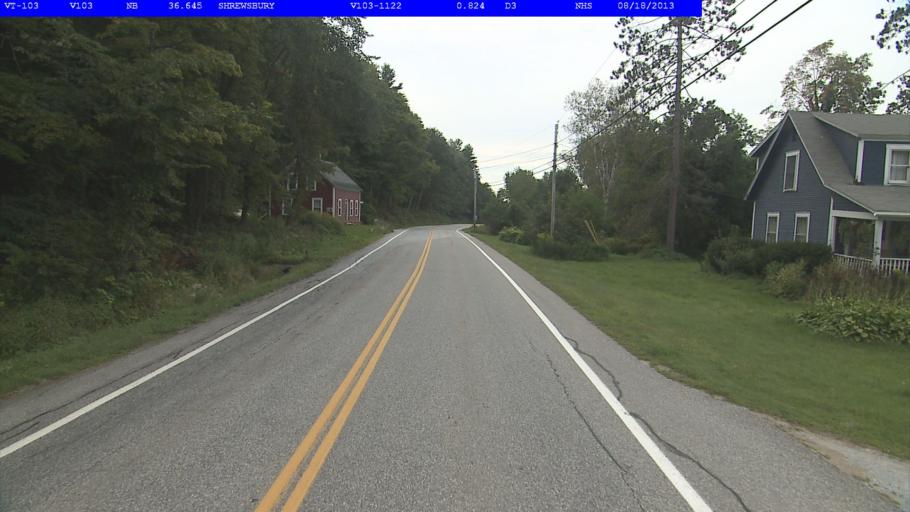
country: US
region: Vermont
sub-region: Rutland County
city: Rutland
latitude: 43.4829
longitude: -72.9005
